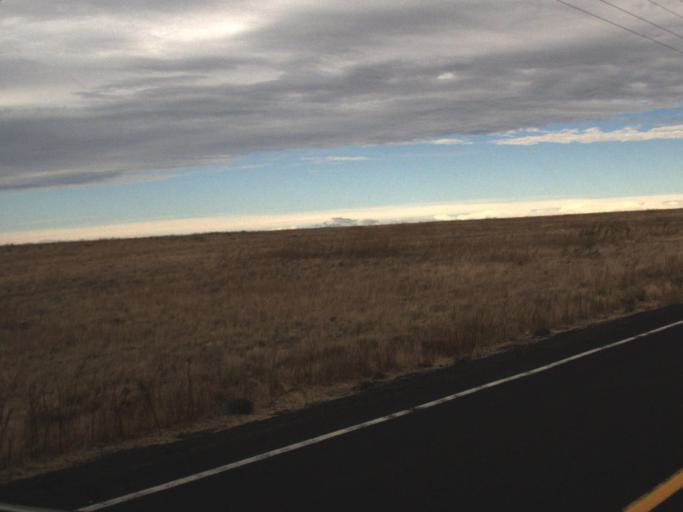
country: US
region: Washington
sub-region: Adams County
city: Ritzville
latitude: 47.4370
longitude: -118.7254
